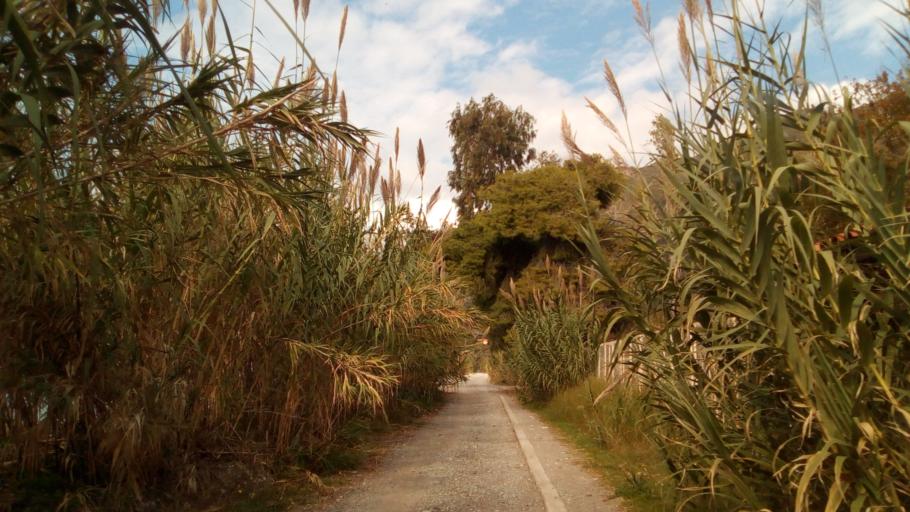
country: GR
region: West Greece
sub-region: Nomos Achaias
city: Kamarai
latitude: 38.3935
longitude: 21.9982
